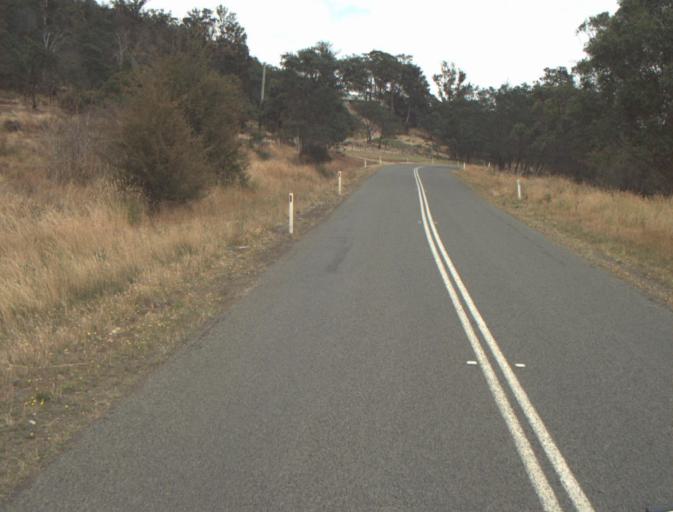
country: AU
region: Tasmania
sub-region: Northern Midlands
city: Evandale
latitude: -41.4989
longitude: 147.4130
